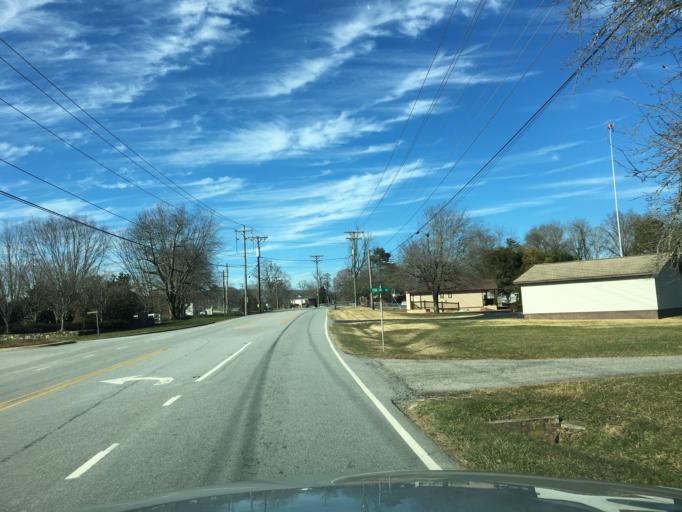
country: US
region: North Carolina
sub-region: Henderson County
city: Mills River
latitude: 35.4062
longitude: -82.5438
